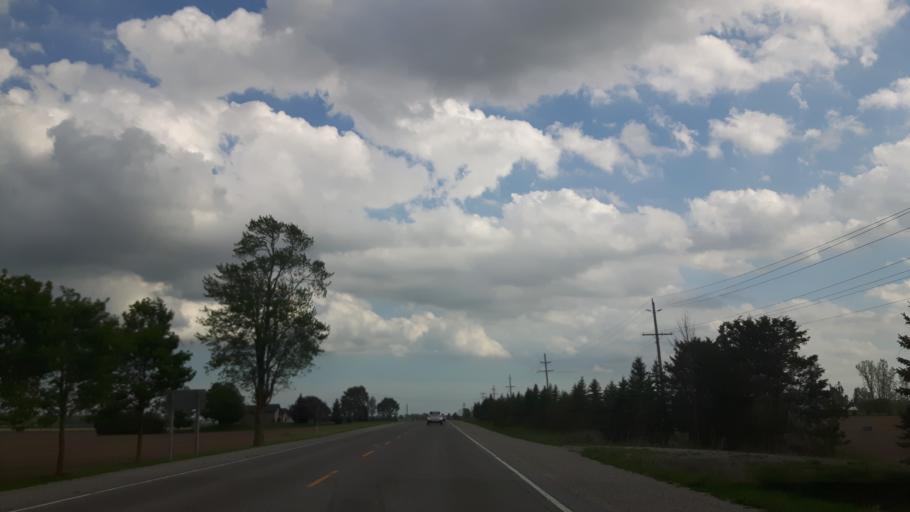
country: CA
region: Ontario
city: South Huron
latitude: 43.2817
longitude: -81.4676
